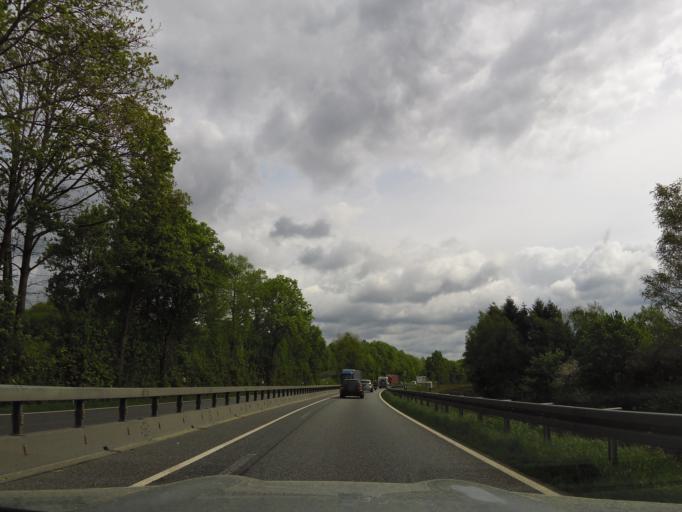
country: DE
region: Hesse
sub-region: Regierungsbezirk Giessen
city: Lohnberg
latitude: 50.5246
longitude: 8.2778
